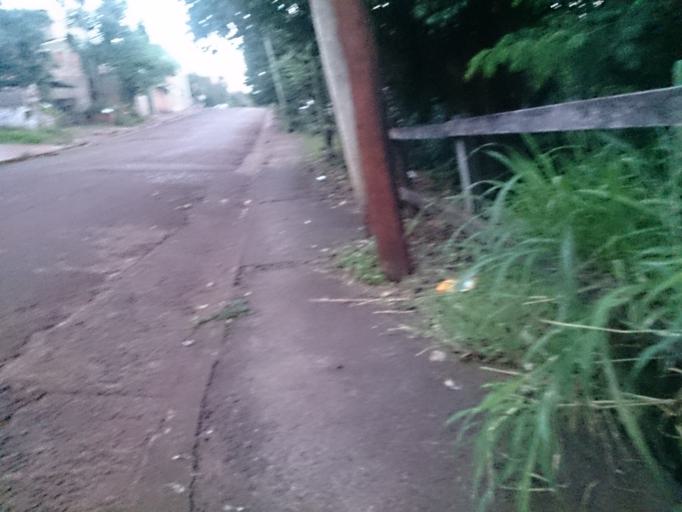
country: AR
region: Misiones
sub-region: Departamento de Obera
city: Obera
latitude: -27.4902
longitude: -55.1245
